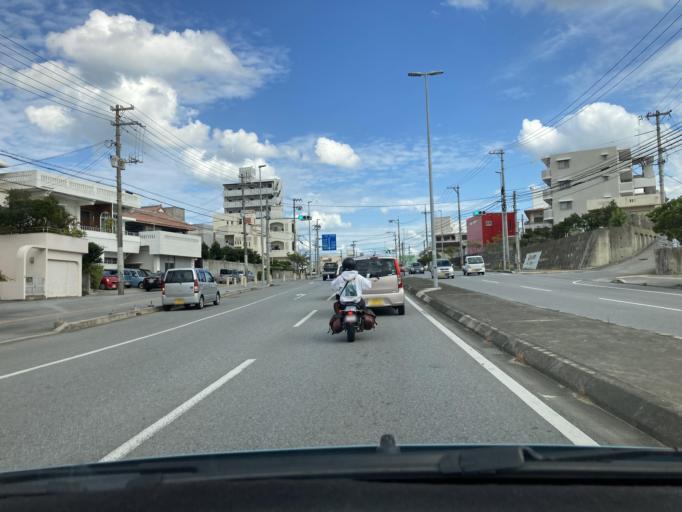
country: JP
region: Okinawa
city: Okinawa
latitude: 26.3607
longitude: 127.8116
